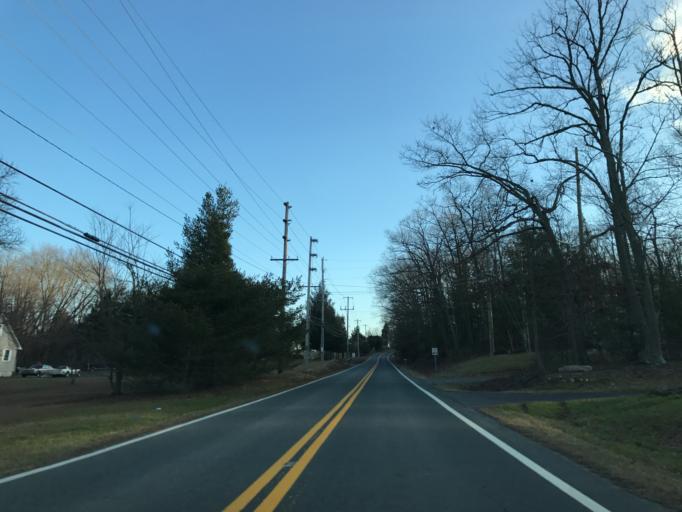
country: US
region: Maryland
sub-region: Cecil County
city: Charlestown
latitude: 39.5165
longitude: -75.9530
